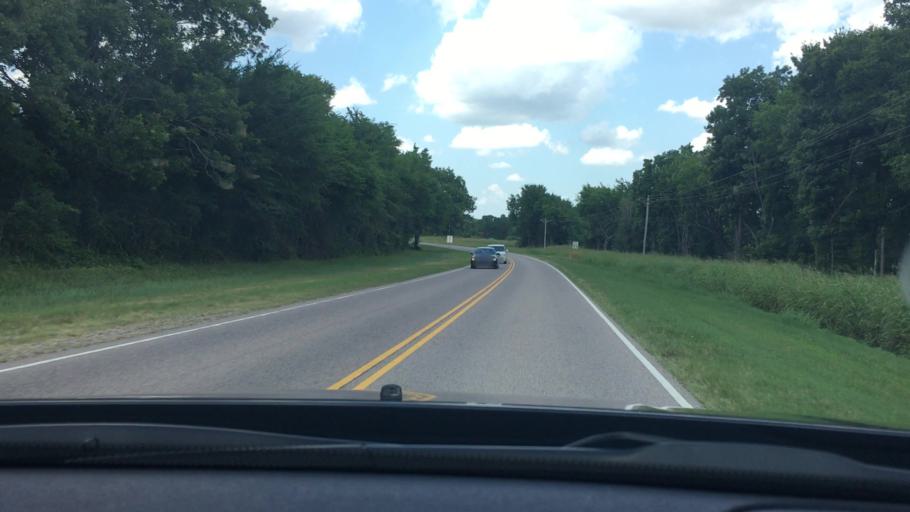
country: US
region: Oklahoma
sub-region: Johnston County
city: Tishomingo
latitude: 34.4815
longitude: -96.6281
